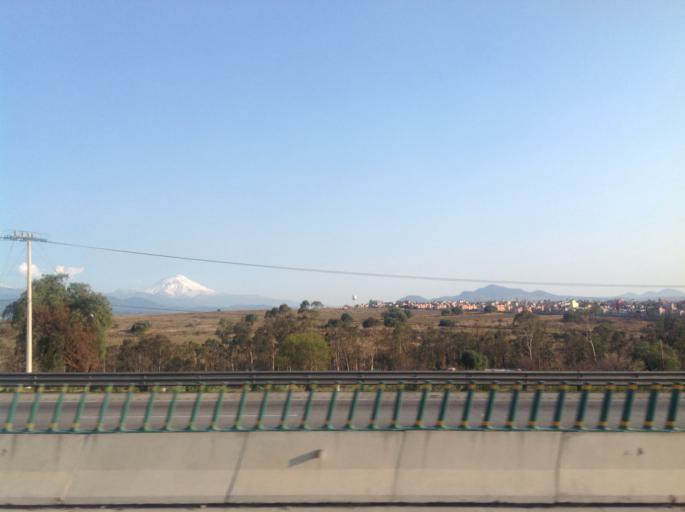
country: MX
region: Mexico
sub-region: Ixtapaluca
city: Jorge Jimenez Cantu
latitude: 19.3060
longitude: -98.8382
